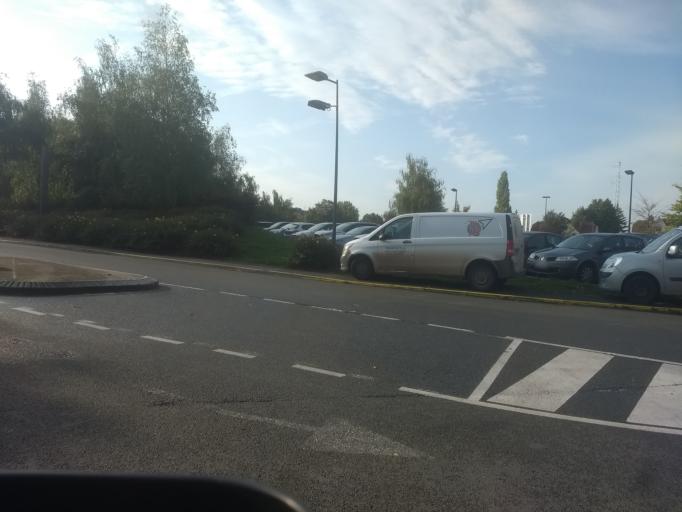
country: FR
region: Nord-Pas-de-Calais
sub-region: Departement du Pas-de-Calais
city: Sainte-Catherine
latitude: 50.2948
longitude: 2.7567
